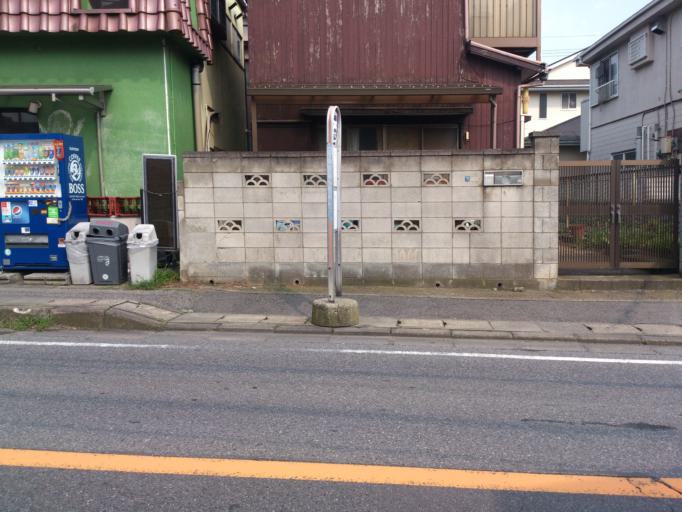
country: JP
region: Chiba
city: Kashiwa
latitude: 35.8336
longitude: 139.9455
